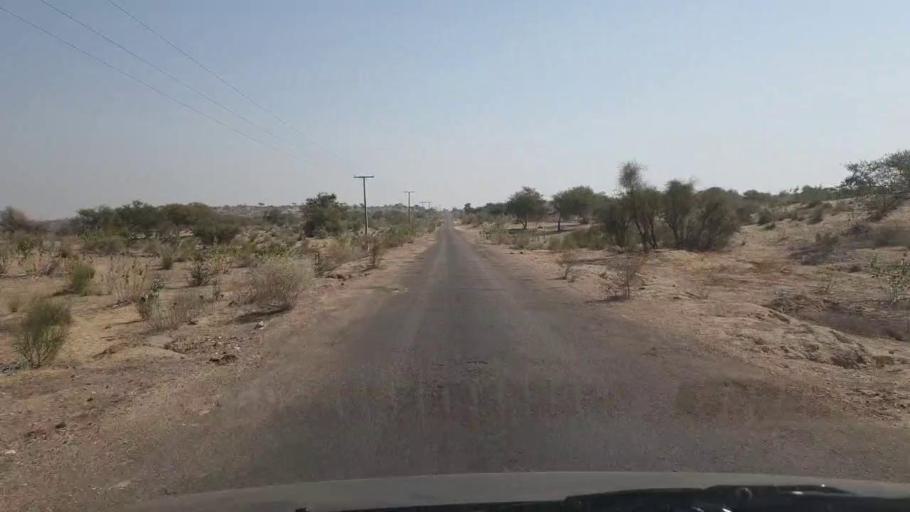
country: PK
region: Sindh
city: Chor
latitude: 25.5947
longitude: 69.9635
